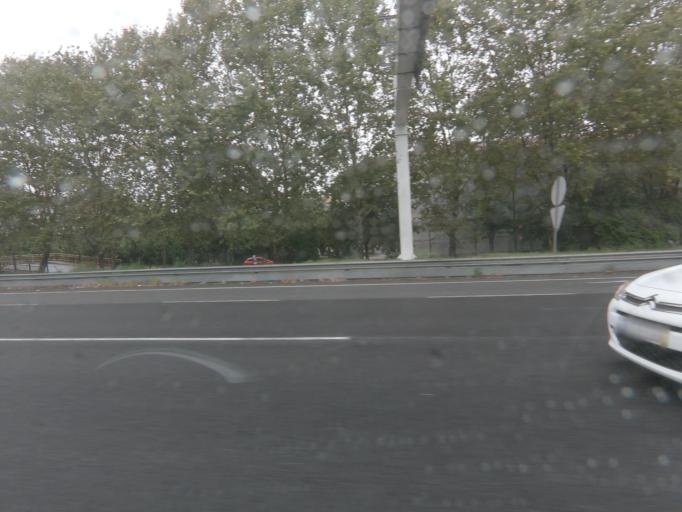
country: PT
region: Porto
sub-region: Porto
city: Porto
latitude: 41.1738
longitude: -8.6188
